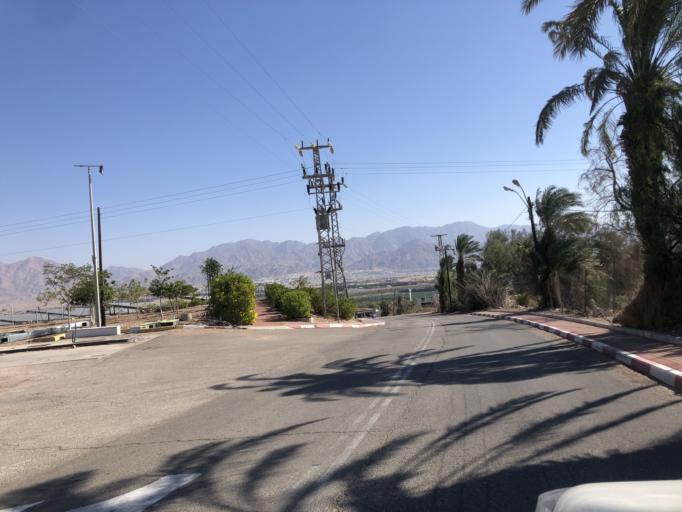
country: IL
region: Southern District
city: Eilat
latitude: 29.5796
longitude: 34.9648
